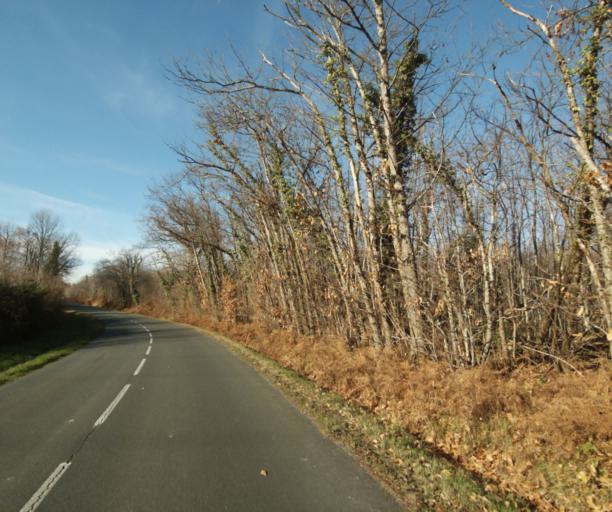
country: FR
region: Poitou-Charentes
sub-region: Departement de la Charente-Maritime
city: Ecoyeux
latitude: 45.7667
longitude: -0.5102
